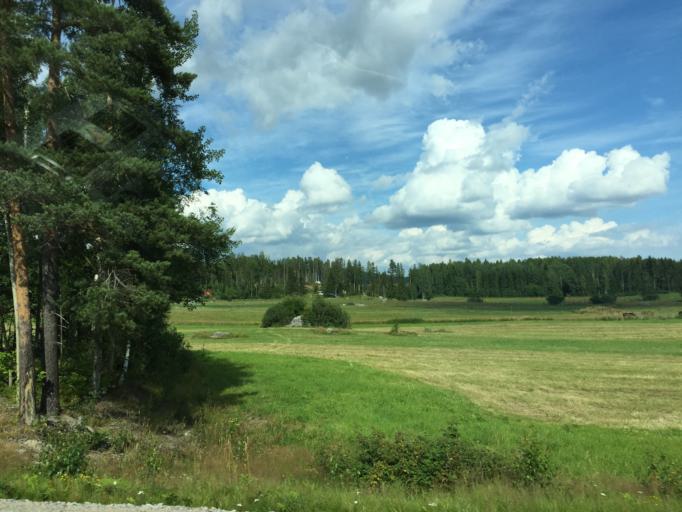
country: SE
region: Gaevleborg
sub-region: Bollnas Kommun
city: Kilafors
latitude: 61.1769
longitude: 16.7921
